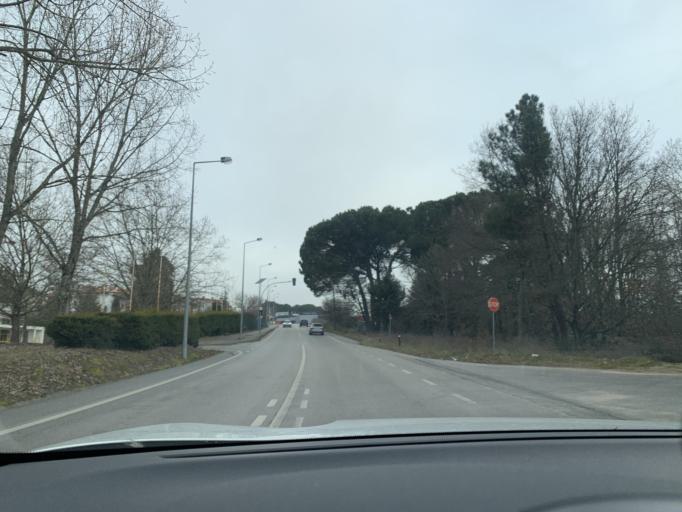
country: PT
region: Viseu
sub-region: Viseu
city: Viseu
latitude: 40.6305
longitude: -7.9031
